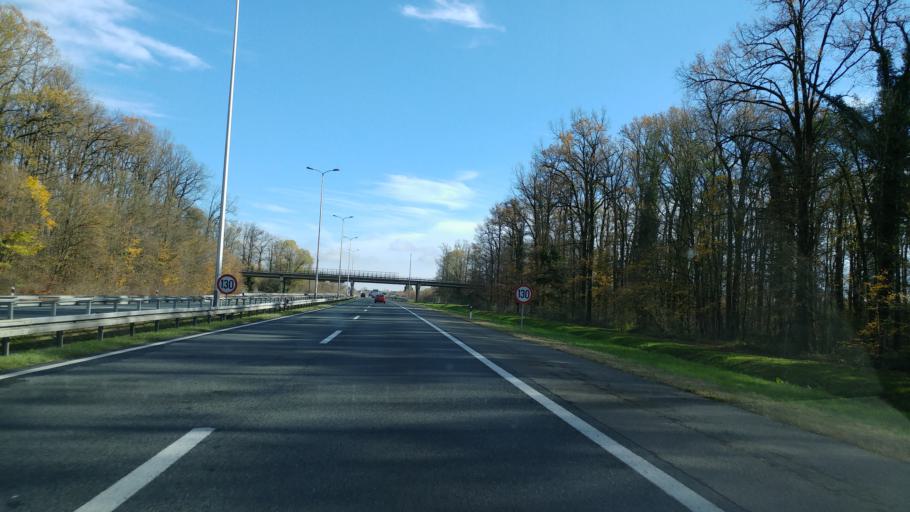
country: HR
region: Sisacko-Moslavacka
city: Novska
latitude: 45.3285
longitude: 16.9465
